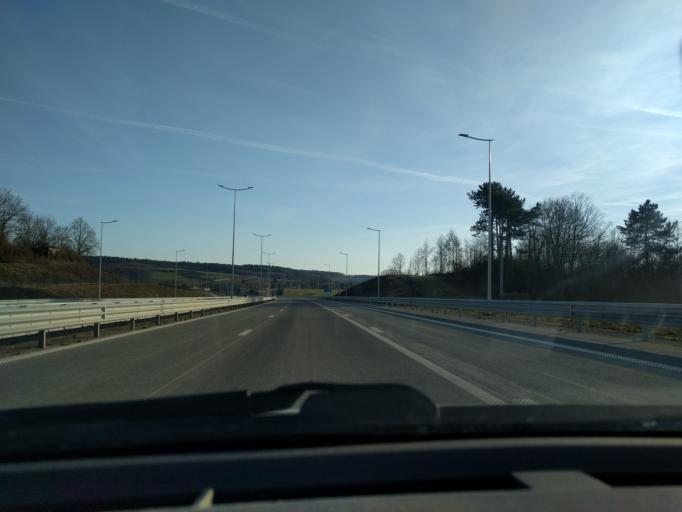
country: BE
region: Wallonia
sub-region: Province de Namur
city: Couvin
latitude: 50.0593
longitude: 4.5057
